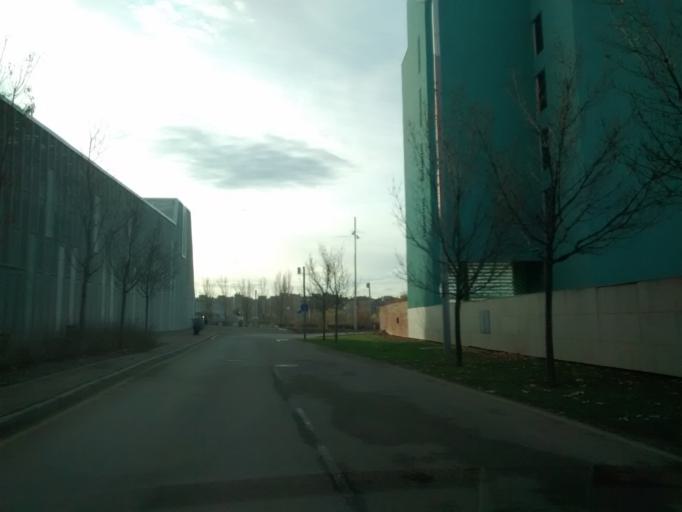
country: ES
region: Aragon
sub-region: Provincia de Zaragoza
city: Almozara
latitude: 41.6686
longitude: -0.9070
